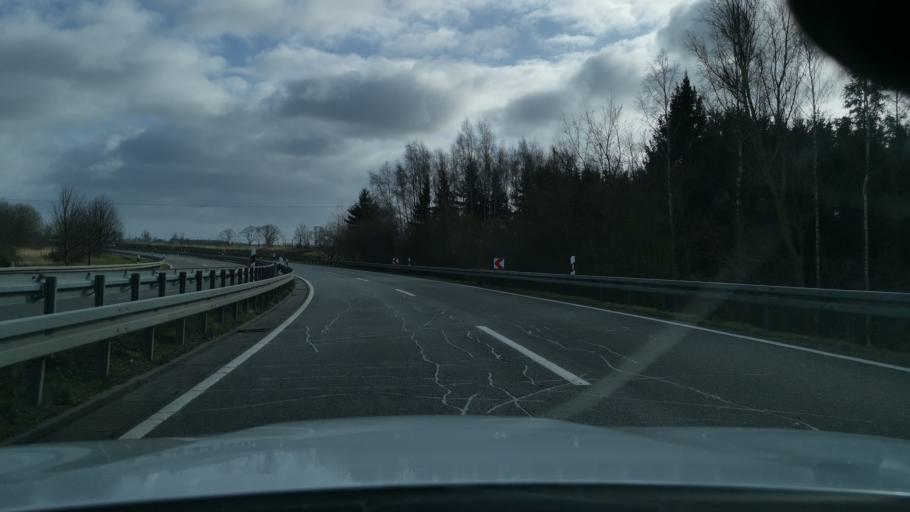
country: DE
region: Mecklenburg-Vorpommern
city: Ziesendorf
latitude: 54.0169
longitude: 12.0610
